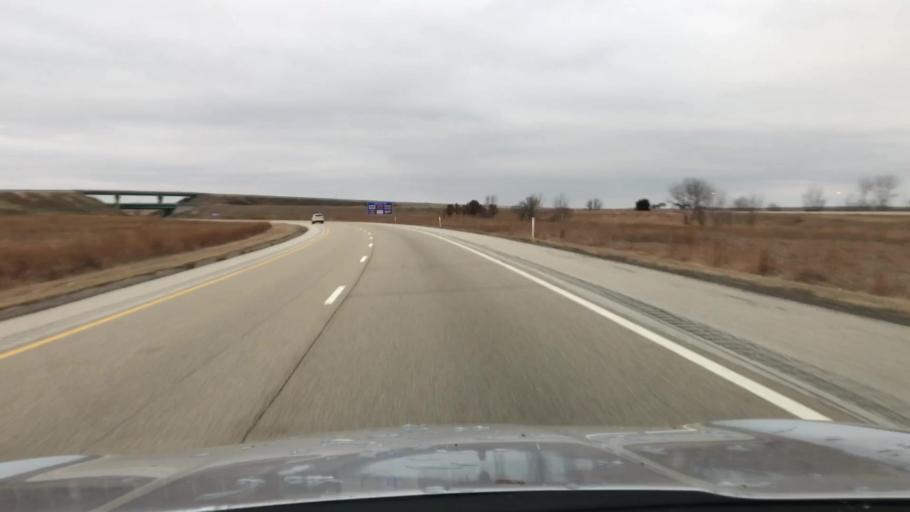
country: US
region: Illinois
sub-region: Logan County
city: Lincoln
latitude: 40.1811
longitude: -89.4112
